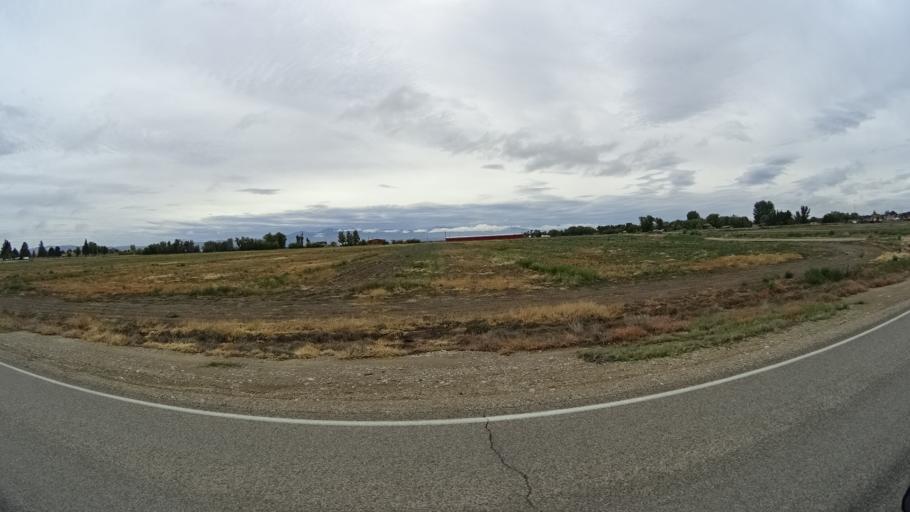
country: US
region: Idaho
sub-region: Ada County
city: Star
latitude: 43.7033
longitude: -116.4736
